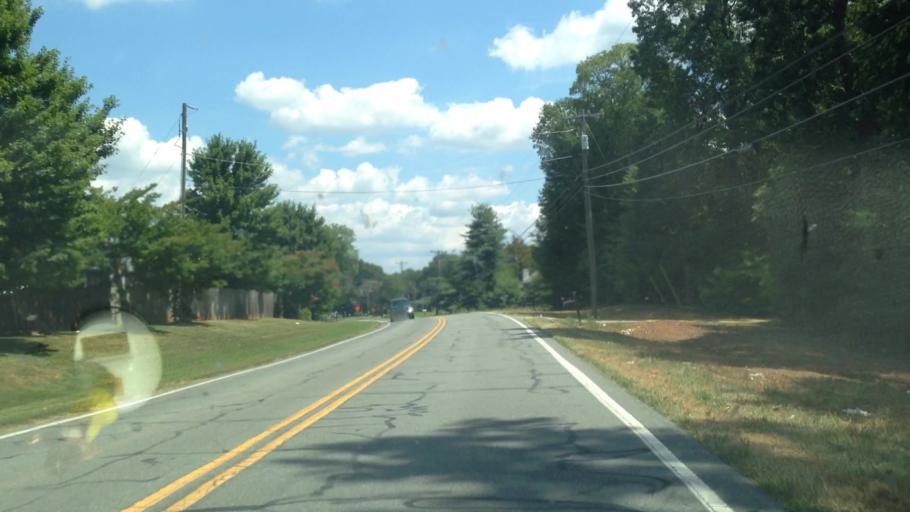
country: US
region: North Carolina
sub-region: Forsyth County
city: Kernersville
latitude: 36.1493
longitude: -80.0635
